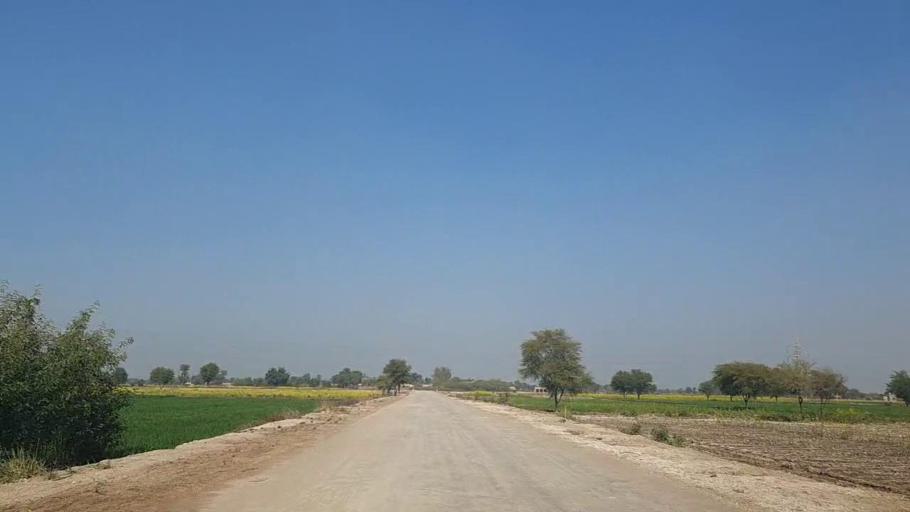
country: PK
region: Sindh
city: Nawabshah
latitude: 26.2232
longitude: 68.3432
